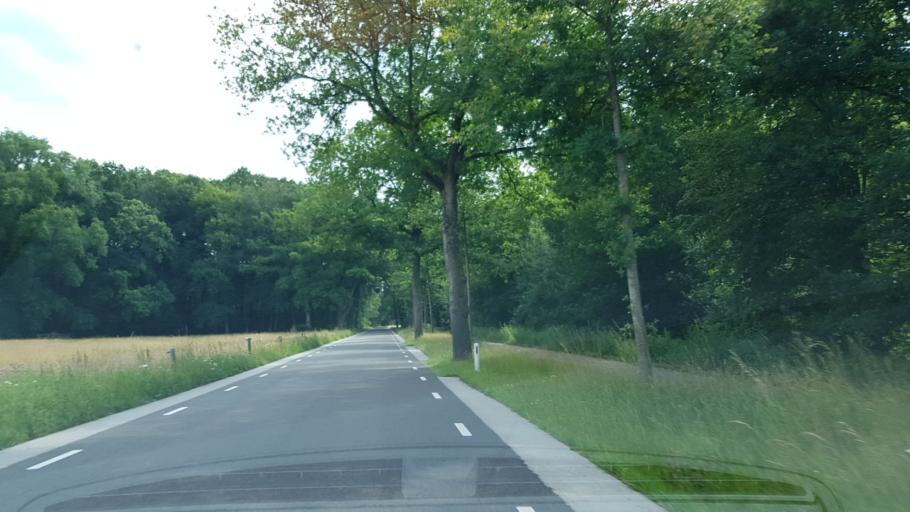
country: NL
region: Gelderland
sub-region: Gemeente Barneveld
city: Garderen
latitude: 52.2812
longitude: 5.7316
